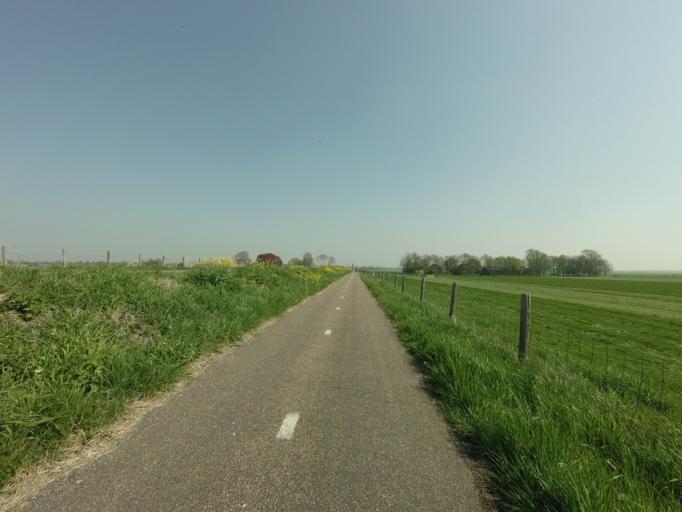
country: NL
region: Utrecht
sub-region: Gemeente De Ronde Venen
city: Mijdrecht
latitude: 52.1886
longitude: 4.8560
